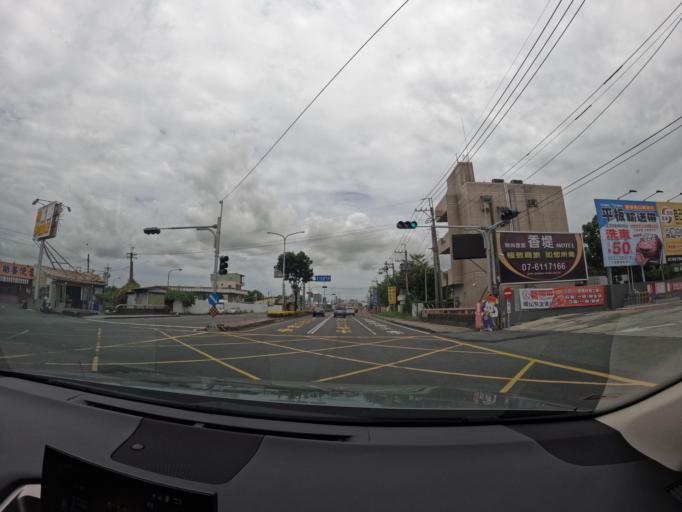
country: TW
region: Taiwan
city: Fengshan
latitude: 22.7869
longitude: 120.3168
